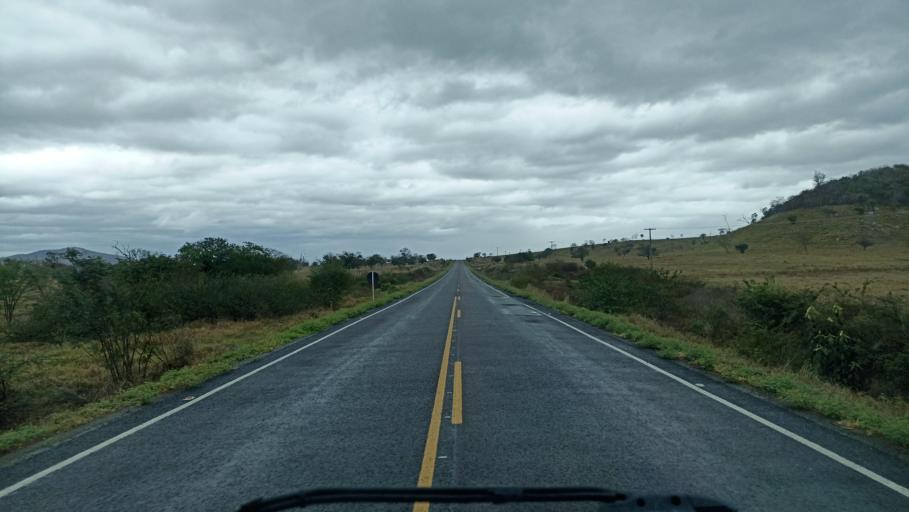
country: BR
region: Bahia
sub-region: Iacu
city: Iacu
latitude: -12.9642
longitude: -40.4858
